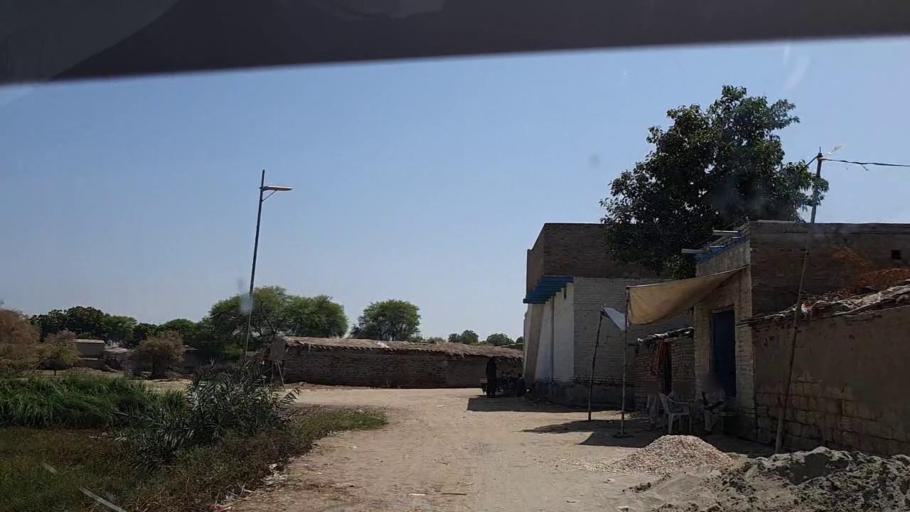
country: PK
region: Sindh
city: Ghauspur
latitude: 28.1392
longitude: 69.0883
